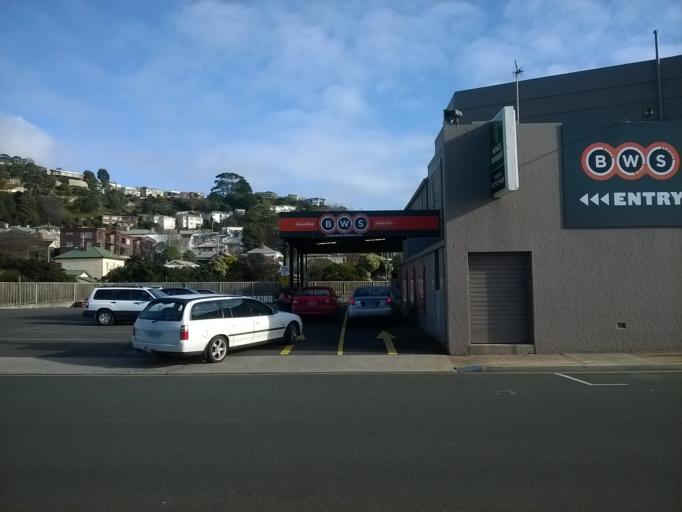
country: AU
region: Tasmania
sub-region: Burnie
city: Burnie
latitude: -41.0487
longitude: 145.9028
